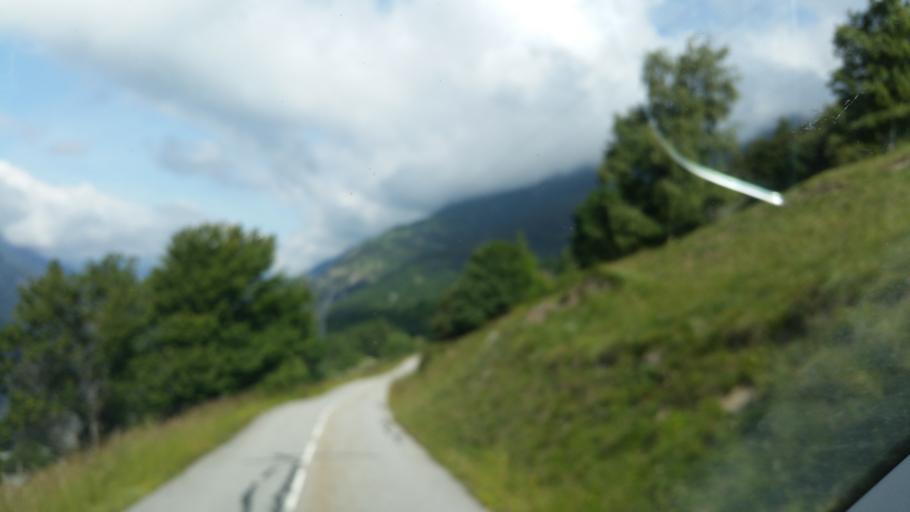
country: FR
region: Rhone-Alpes
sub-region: Departement de la Savoie
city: Modane
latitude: 45.2094
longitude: 6.6095
